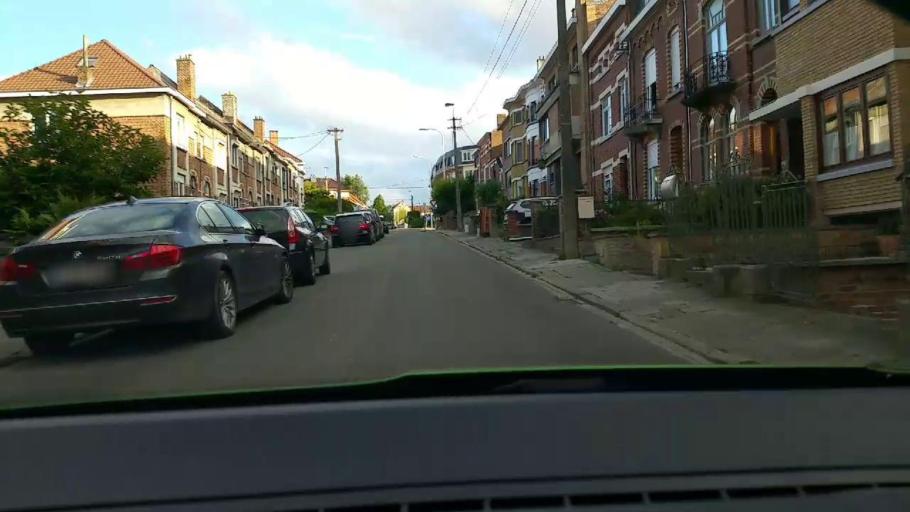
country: BE
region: Wallonia
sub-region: Province du Brabant Wallon
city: Nivelles
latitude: 50.5953
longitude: 4.3315
